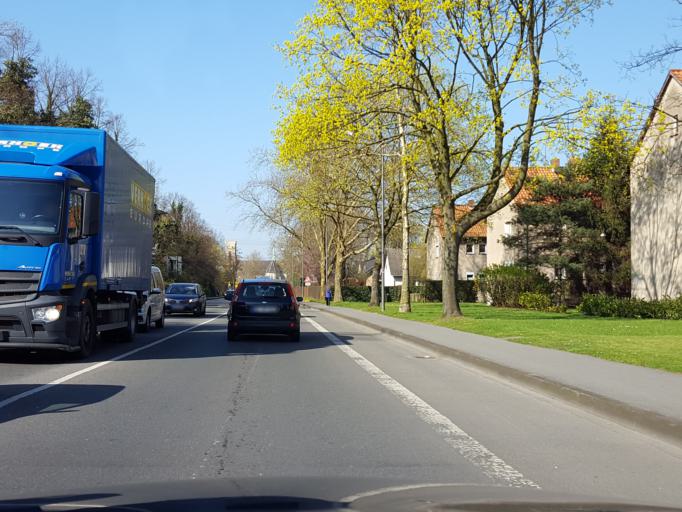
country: DE
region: North Rhine-Westphalia
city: Castrop-Rauxel
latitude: 51.5934
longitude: 7.3109
